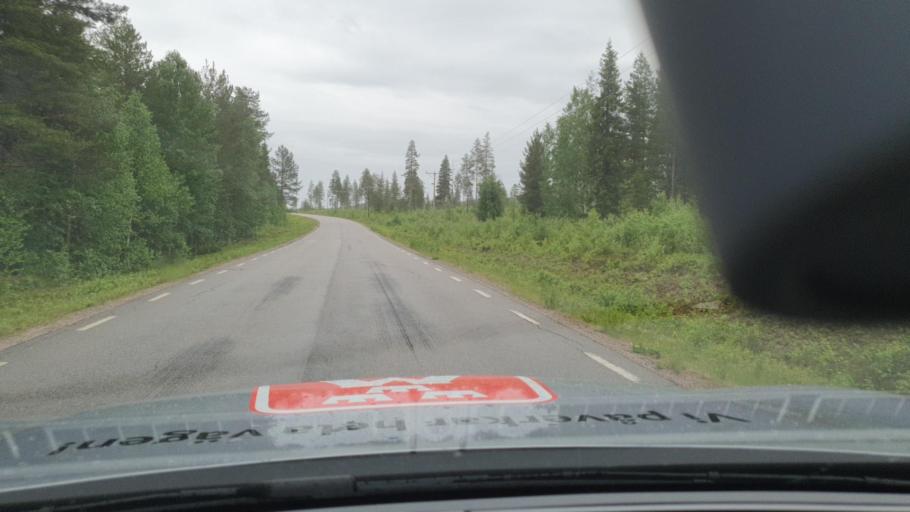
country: SE
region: Norrbotten
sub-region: Pajala Kommun
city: Pajala
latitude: 66.7618
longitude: 23.1544
